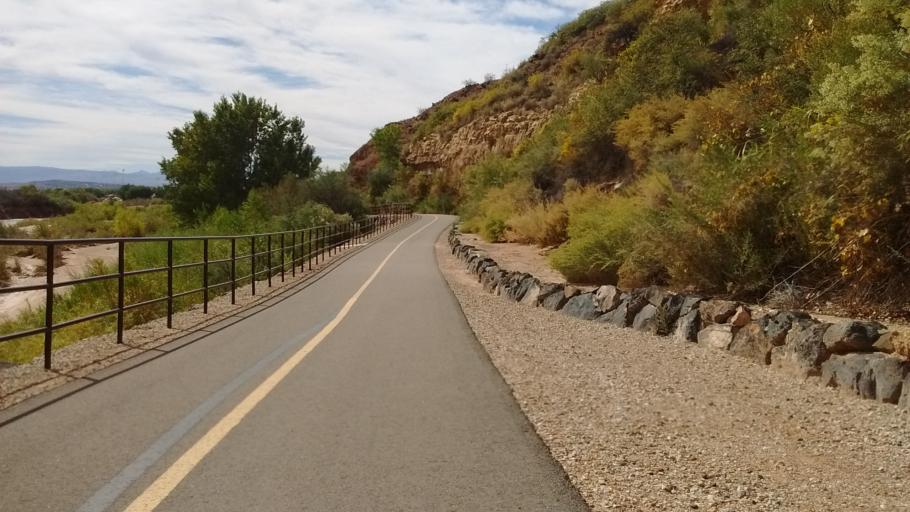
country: US
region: Utah
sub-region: Washington County
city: Washington
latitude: 37.1245
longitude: -113.4941
